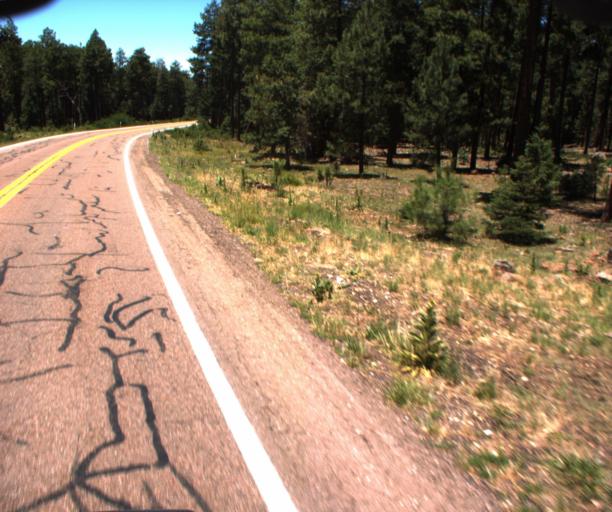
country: US
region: Arizona
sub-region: Gila County
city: Pine
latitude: 34.4553
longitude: -111.4004
